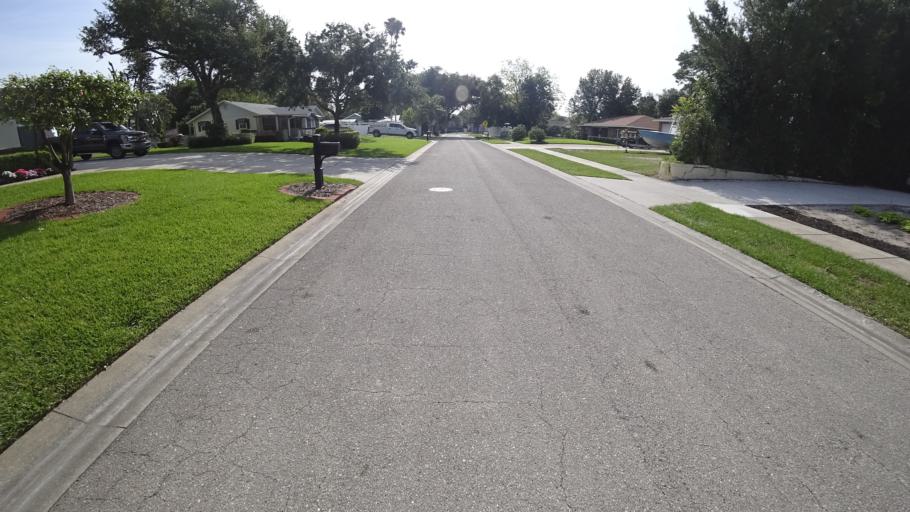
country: US
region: Florida
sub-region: Manatee County
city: West Bradenton
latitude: 27.5052
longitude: -82.6336
